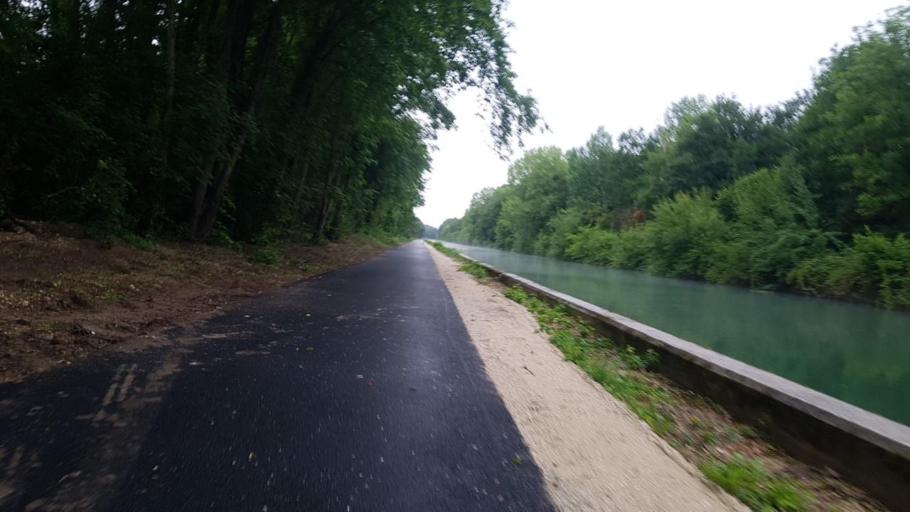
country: FR
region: Champagne-Ardenne
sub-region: Departement de la Marne
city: Sarry
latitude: 48.8642
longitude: 4.4717
